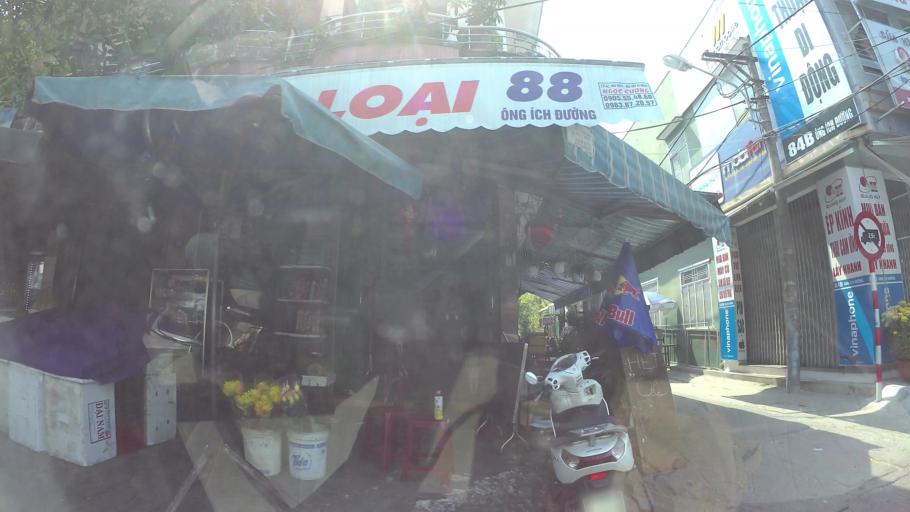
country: VN
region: Da Nang
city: Cam Le
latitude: 16.0153
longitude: 108.2051
